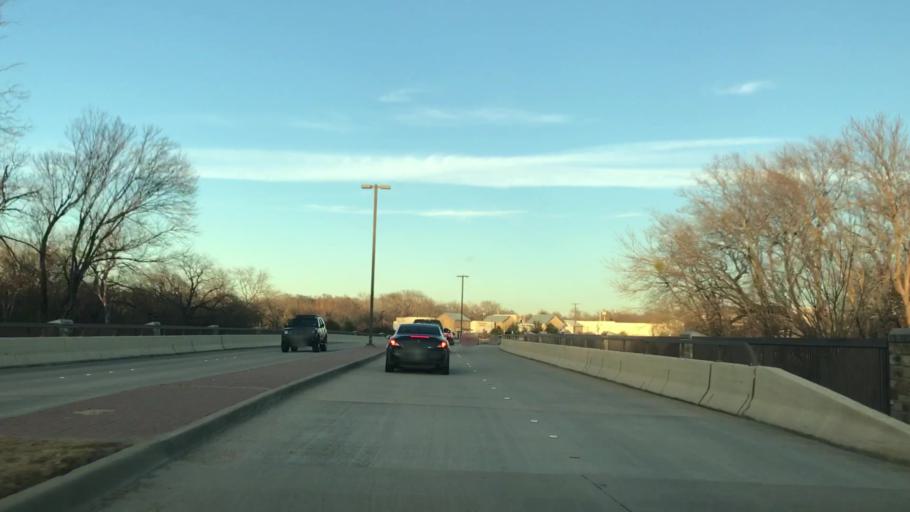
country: US
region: Texas
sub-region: Rockwall County
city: Rockwall
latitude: 32.9492
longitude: -96.4656
